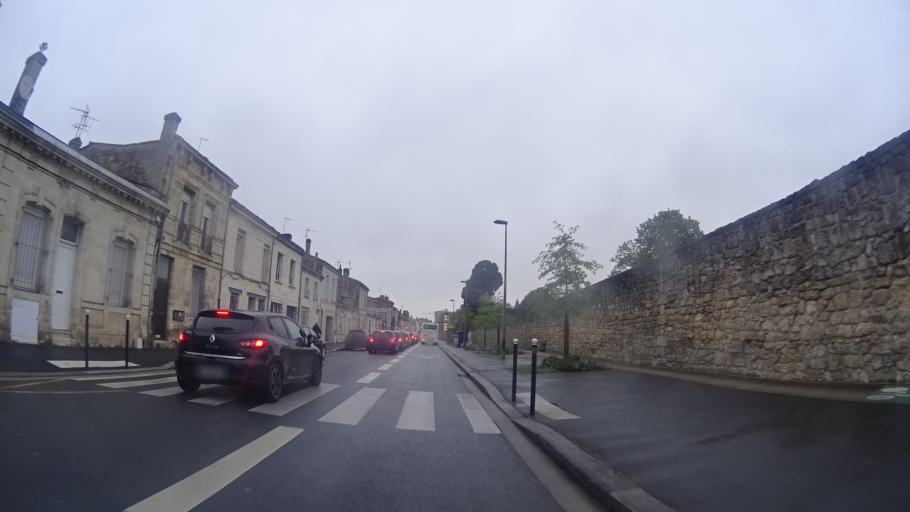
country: FR
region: Aquitaine
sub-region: Departement de la Gironde
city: Bordeaux
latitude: 44.8371
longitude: -0.5947
